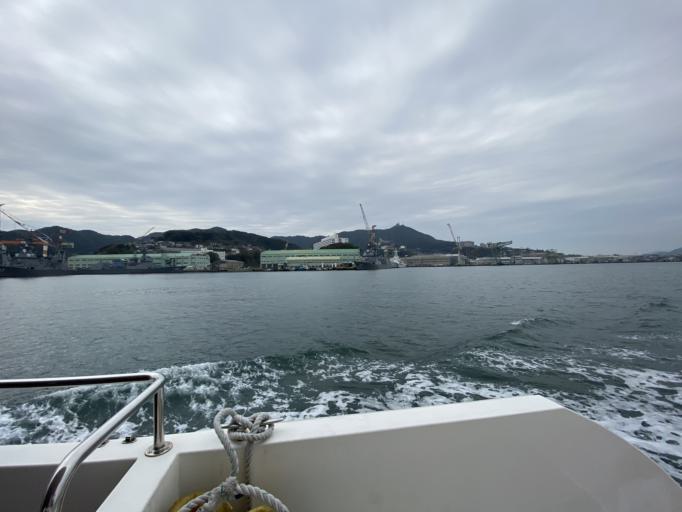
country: JP
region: Nagasaki
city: Nagasaki-shi
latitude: 32.7349
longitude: 129.8609
